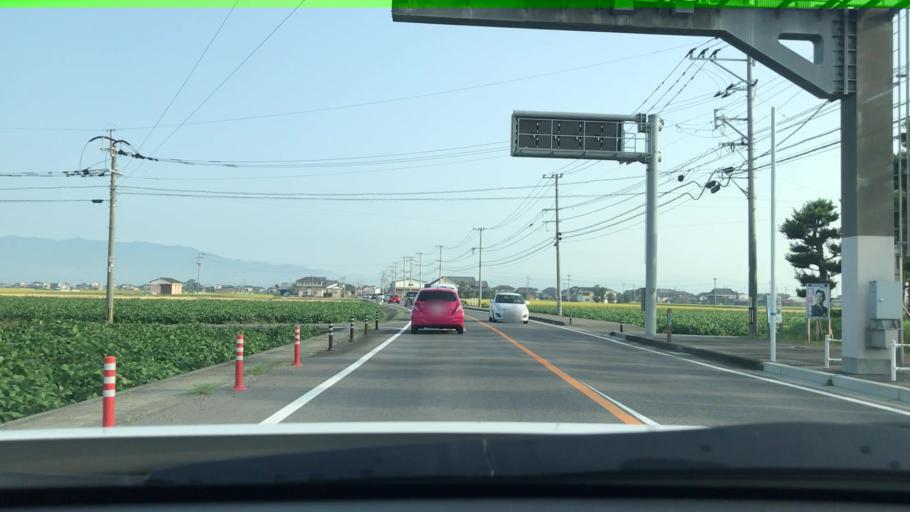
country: JP
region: Saga Prefecture
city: Saga-shi
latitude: 33.2042
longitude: 130.2054
